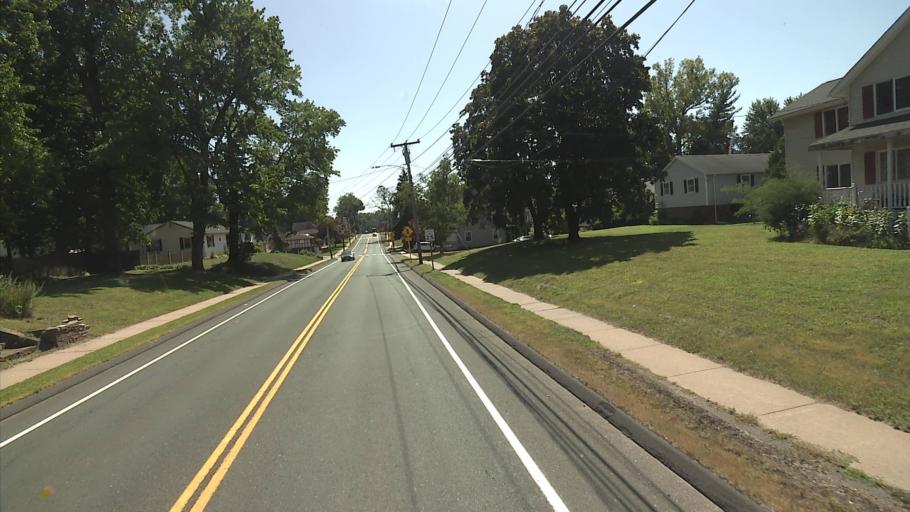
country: US
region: Connecticut
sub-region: Hartford County
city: Windsor Locks
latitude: 41.9394
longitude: -72.6296
